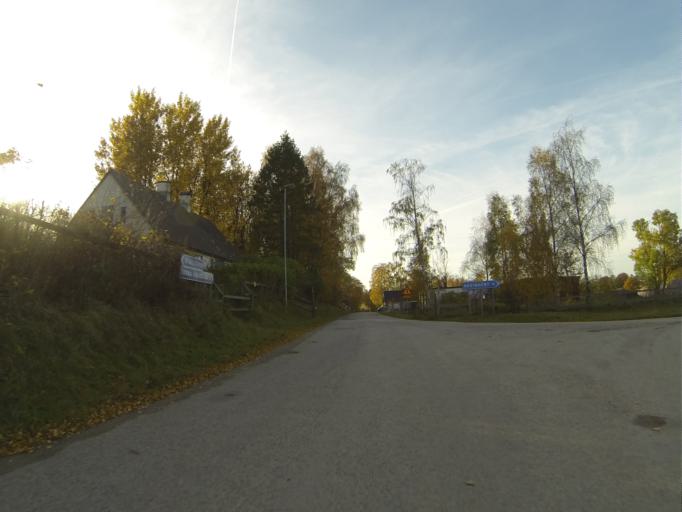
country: SE
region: Skane
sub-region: Lunds Kommun
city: Veberod
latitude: 55.6979
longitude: 13.4288
